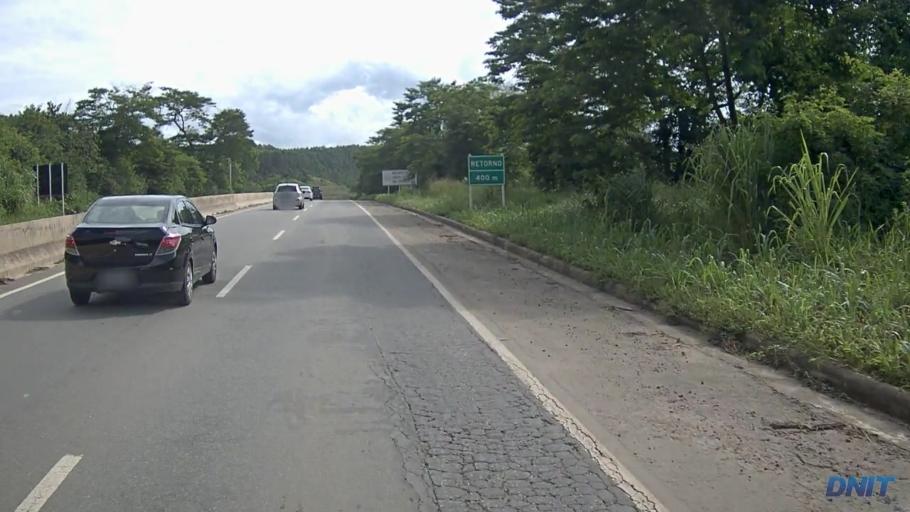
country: BR
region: Minas Gerais
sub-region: Ipaba
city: Ipaba
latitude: -19.3183
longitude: -42.4028
